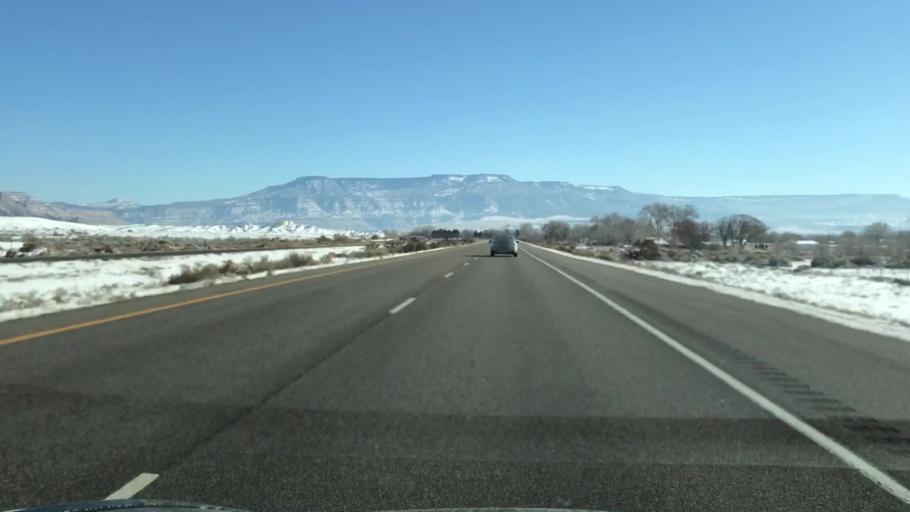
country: US
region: Colorado
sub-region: Mesa County
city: Fruitvale
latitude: 39.1066
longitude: -108.4923
